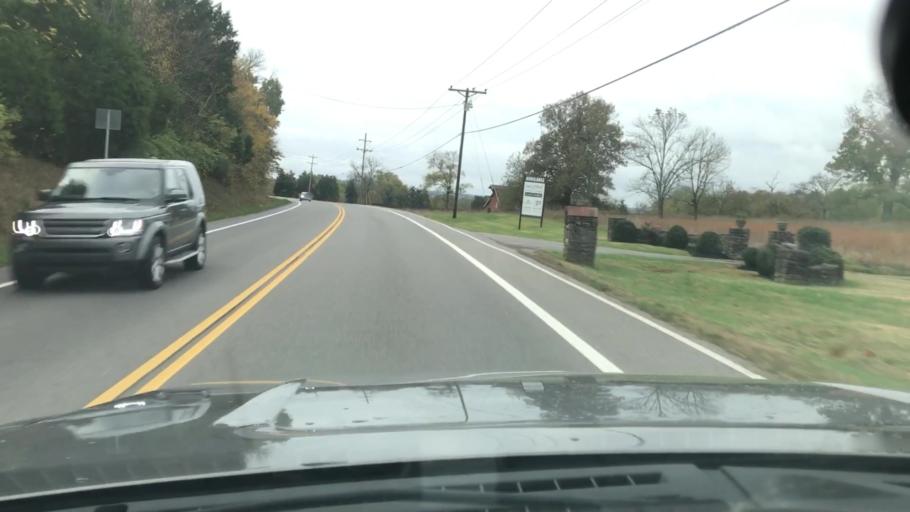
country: US
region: Tennessee
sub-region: Williamson County
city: Franklin
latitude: 35.9882
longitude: -86.8908
